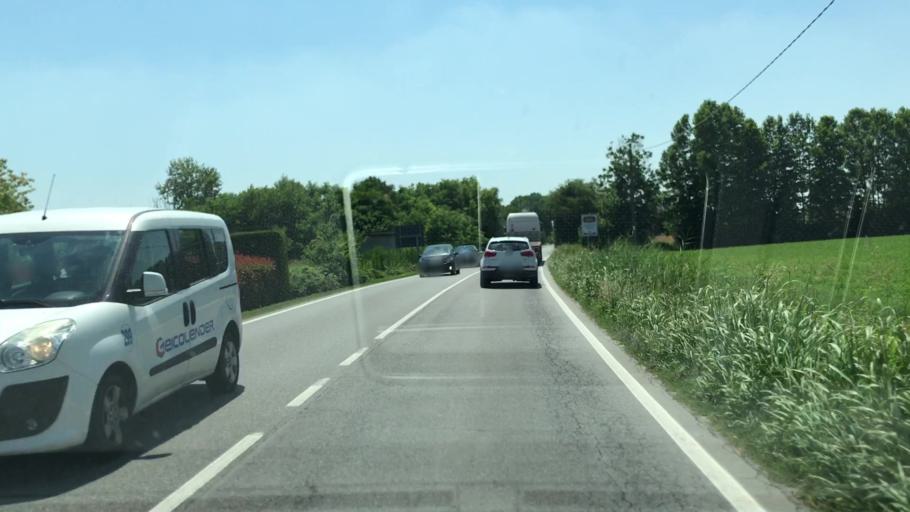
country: IT
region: Lombardy
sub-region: Provincia di Mantova
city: Pegognaga
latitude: 44.9951
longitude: 10.8778
